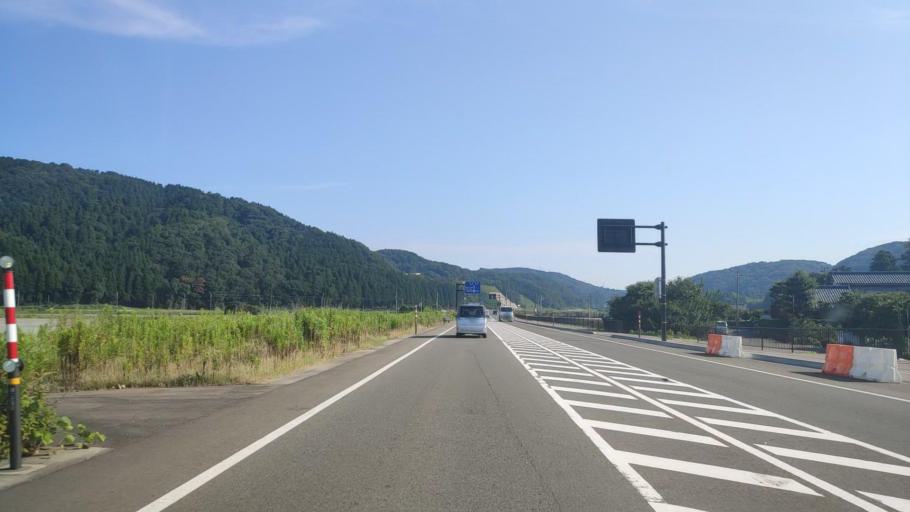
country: JP
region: Fukui
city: Maruoka
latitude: 36.2002
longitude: 136.2674
